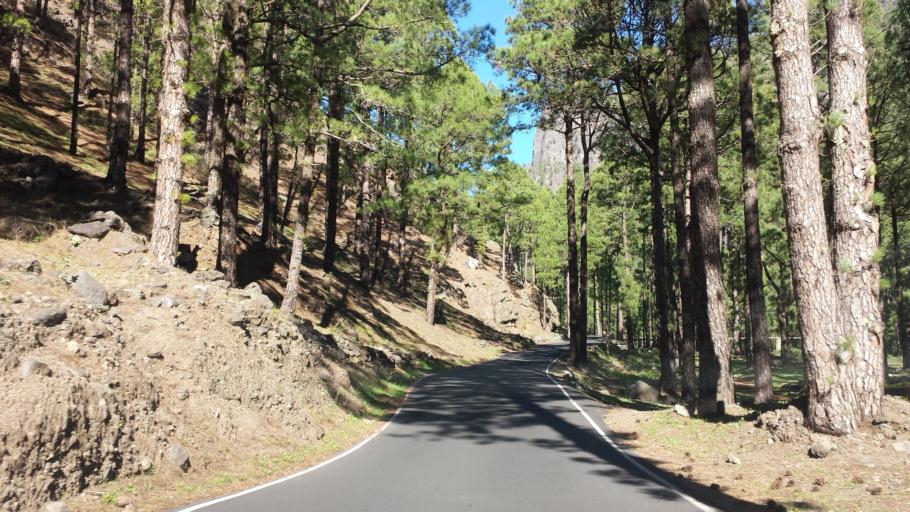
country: ES
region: Canary Islands
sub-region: Provincia de Santa Cruz de Tenerife
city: El Paso
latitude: 28.6797
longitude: -17.8470
